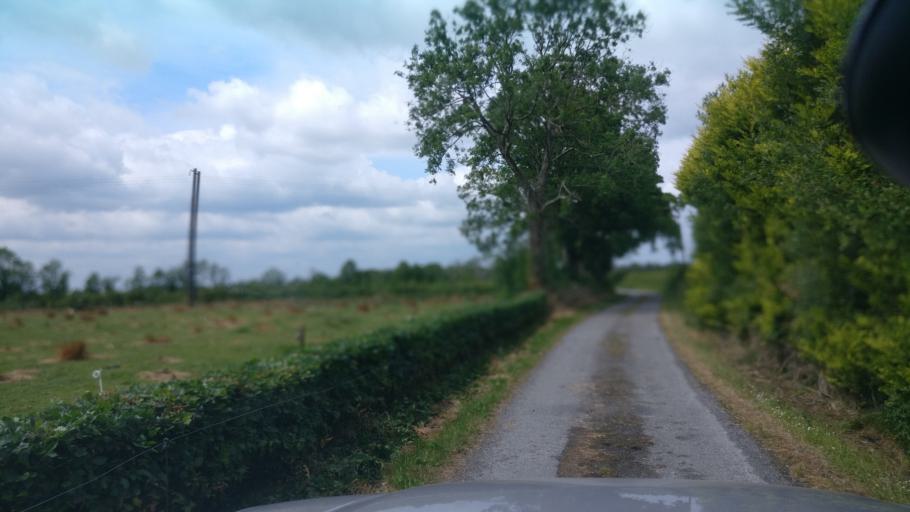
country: IE
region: Connaught
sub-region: County Galway
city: Ballinasloe
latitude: 53.2727
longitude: -8.3348
